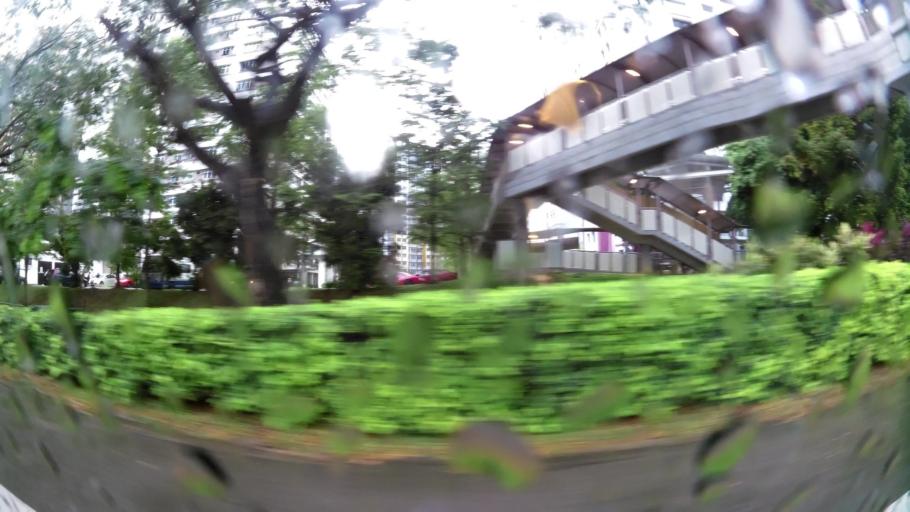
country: MY
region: Johor
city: Kampung Pasir Gudang Baru
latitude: 1.3914
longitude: 103.9094
